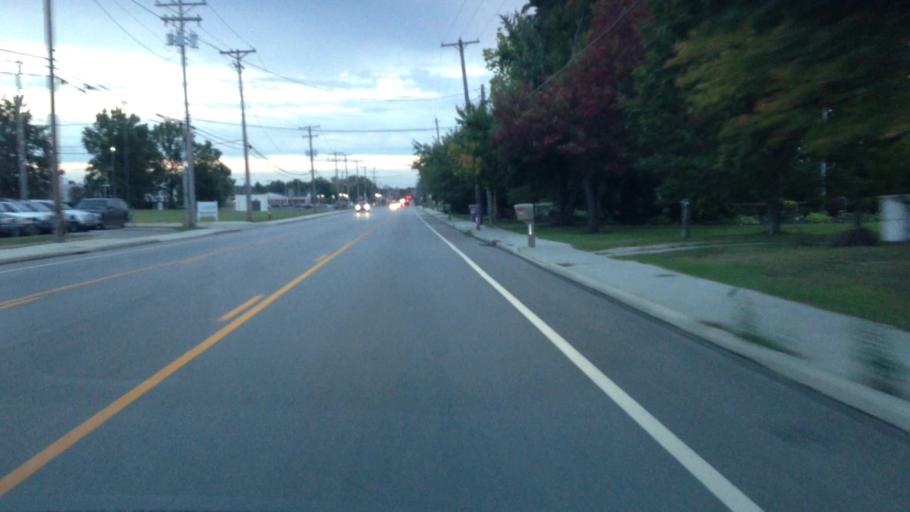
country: US
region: Ohio
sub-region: Summit County
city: Cuyahoga Falls
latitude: 41.1766
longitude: -81.5086
